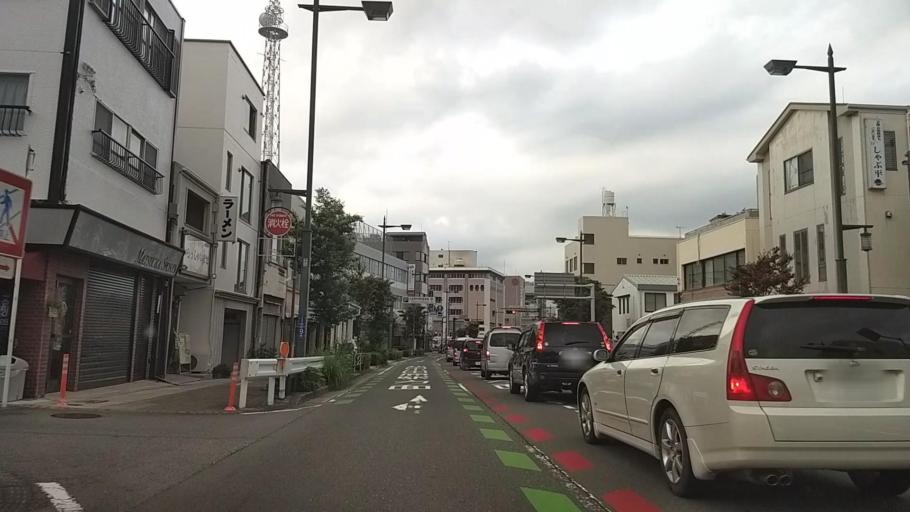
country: JP
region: Kanagawa
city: Odawara
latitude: 35.2487
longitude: 139.1596
